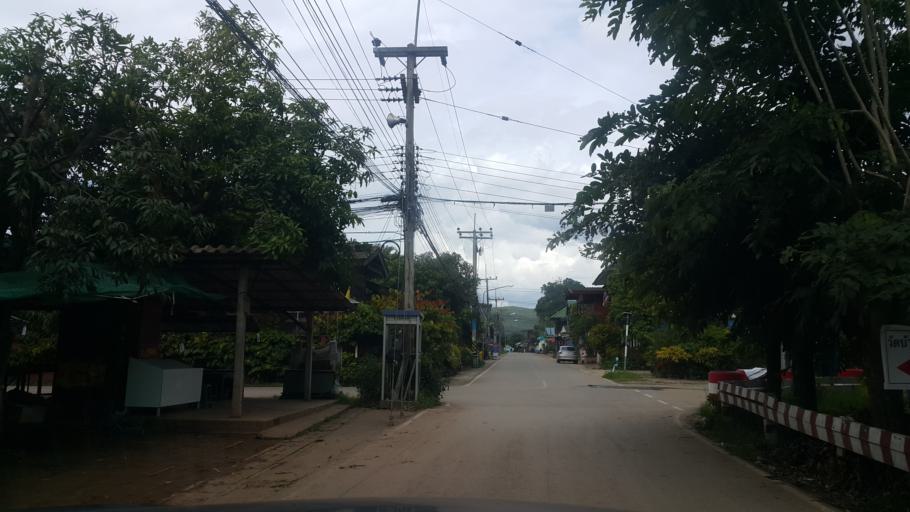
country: TH
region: Chiang Mai
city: Mae Taeng
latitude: 19.1818
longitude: 98.9903
